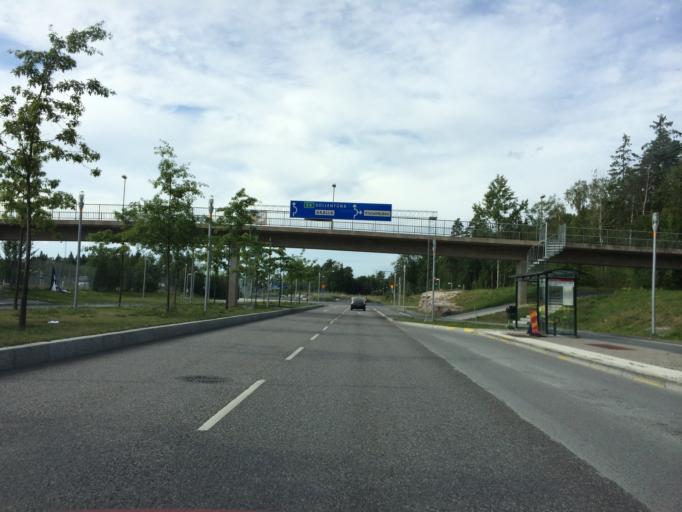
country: SE
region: Stockholm
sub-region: Stockholms Kommun
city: Kista
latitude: 59.4117
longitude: 17.9333
